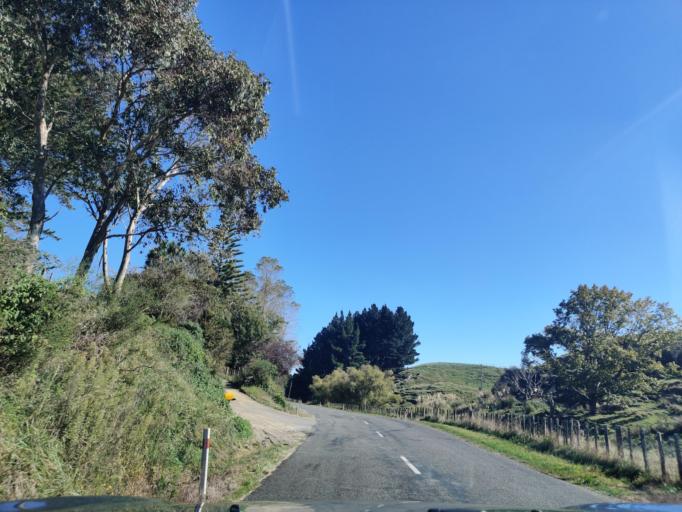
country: NZ
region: Manawatu-Wanganui
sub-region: Palmerston North City
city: Palmerston North
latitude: -40.2562
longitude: 175.6986
